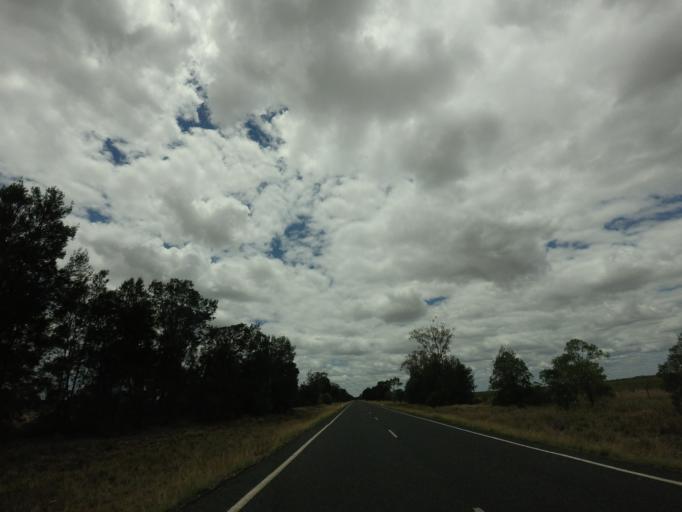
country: AU
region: Queensland
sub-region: Goondiwindi
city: Goondiwindi
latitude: -28.1672
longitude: 150.5232
